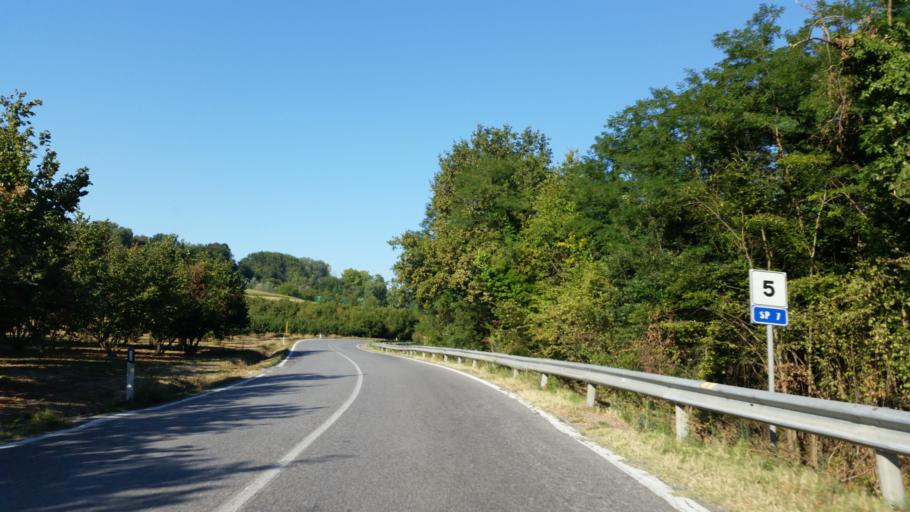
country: IT
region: Piedmont
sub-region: Provincia di Cuneo
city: Verduno
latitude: 44.6815
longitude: 7.9338
